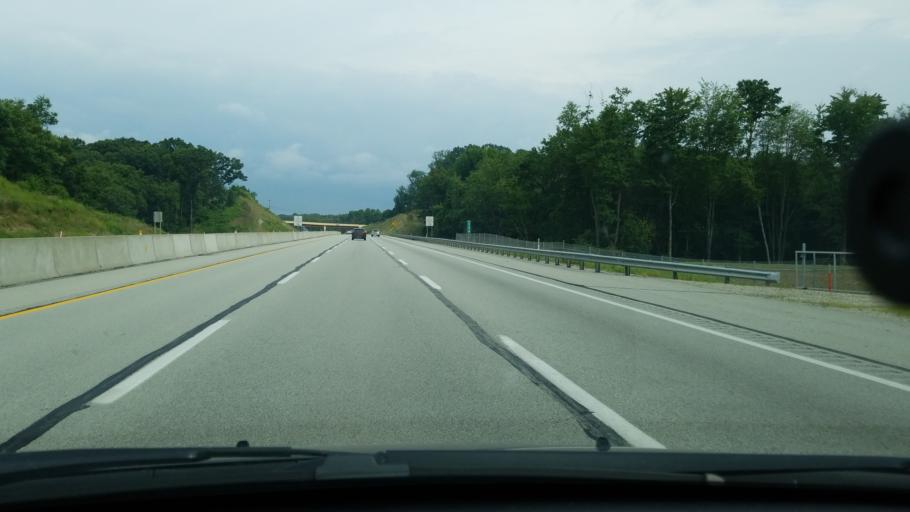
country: US
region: Pennsylvania
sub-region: Allegheny County
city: Gibsonia
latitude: 40.6428
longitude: -80.0141
